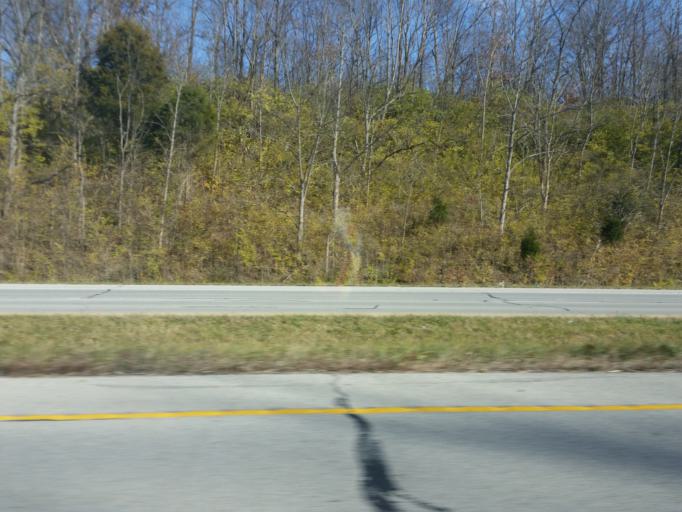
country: US
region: Ohio
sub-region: Hamilton County
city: Dunlap
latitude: 39.2884
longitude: -84.6059
